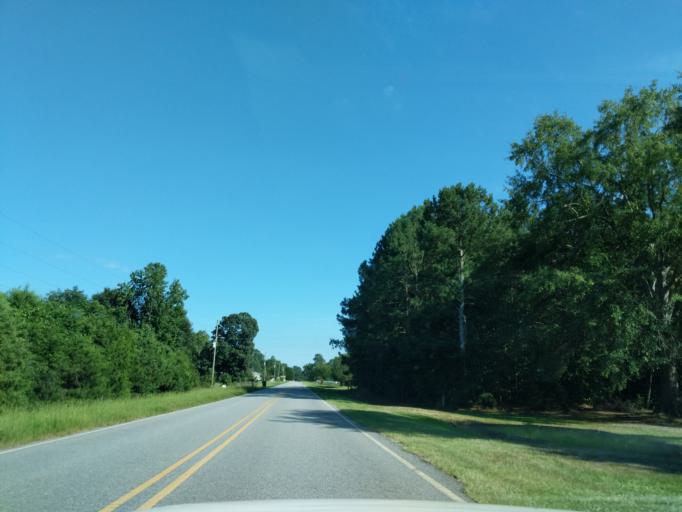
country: US
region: Georgia
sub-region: Oglethorpe County
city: Lexington
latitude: 33.9522
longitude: -83.0711
